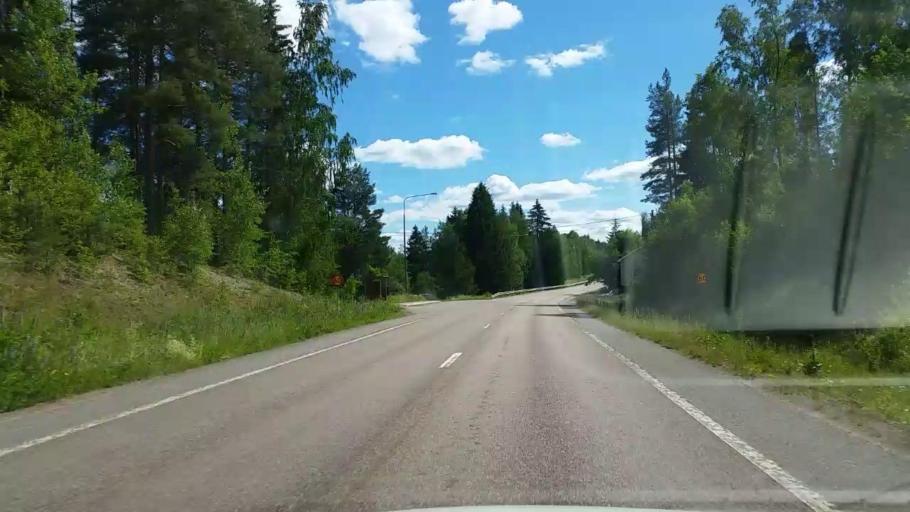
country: SE
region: Dalarna
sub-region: Faluns Kommun
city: Svardsjo
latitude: 60.8329
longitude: 15.7605
